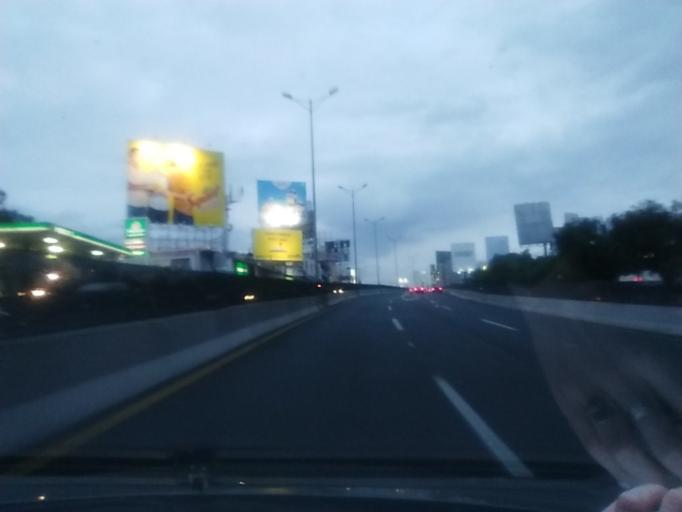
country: MX
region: Mexico
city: Naucalpan de Juarez
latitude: 19.4992
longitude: -99.2373
